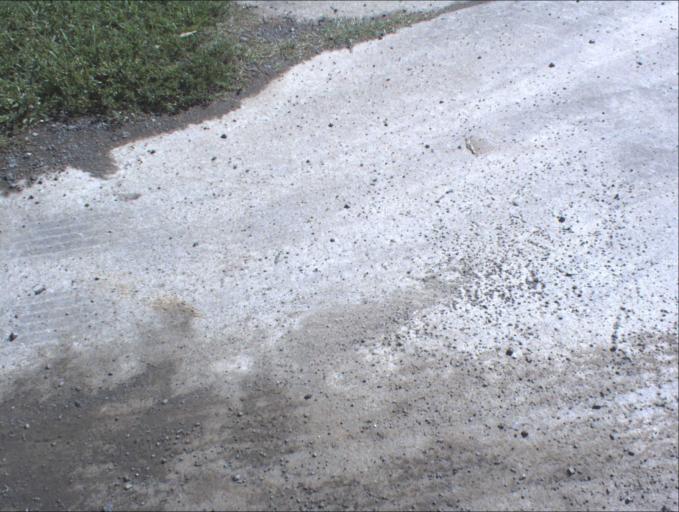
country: AU
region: Queensland
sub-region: Logan
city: North Maclean
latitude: -27.8249
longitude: 153.0314
